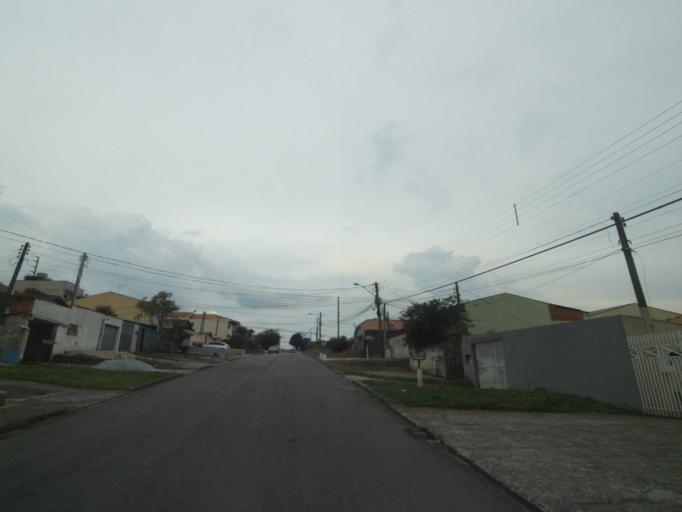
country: BR
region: Parana
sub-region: Pinhais
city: Pinhais
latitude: -25.4038
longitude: -49.2026
